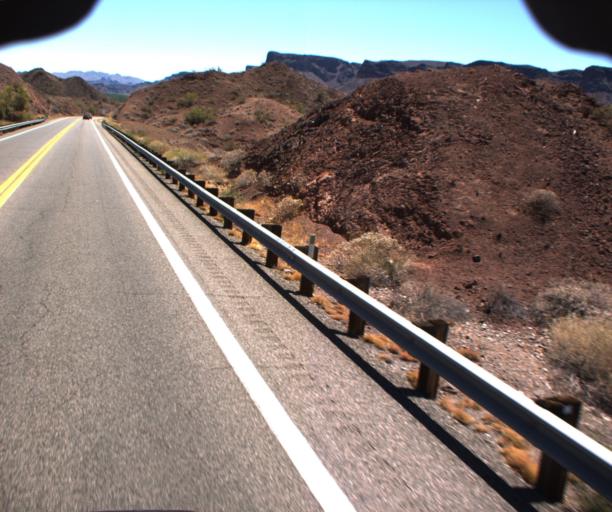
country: US
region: Arizona
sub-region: La Paz County
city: Cienega Springs
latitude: 34.3098
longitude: -114.1026
